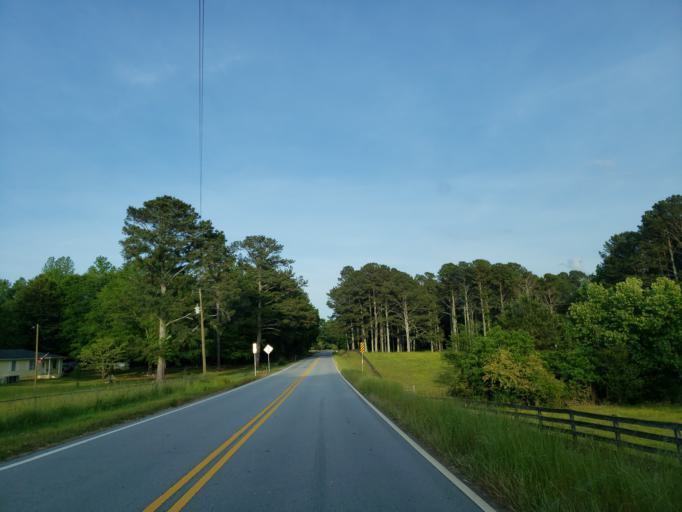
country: US
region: Georgia
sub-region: Carroll County
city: Mount Zion
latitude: 33.6110
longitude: -85.1594
